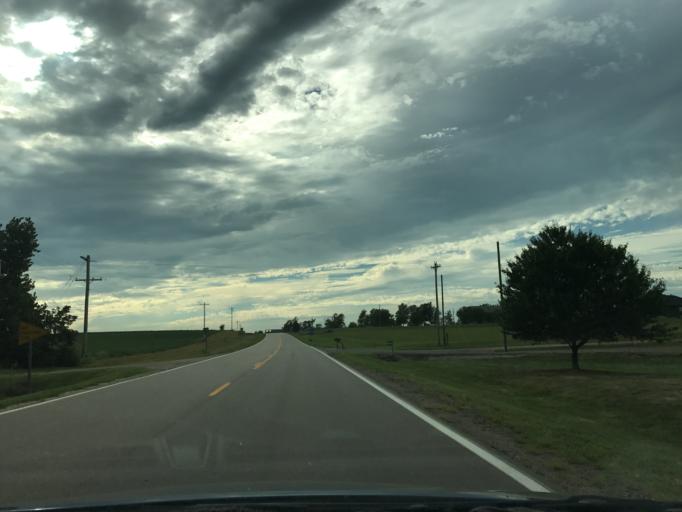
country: US
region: Nebraska
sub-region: Gage County
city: Beatrice
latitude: 40.2835
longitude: -96.8025
